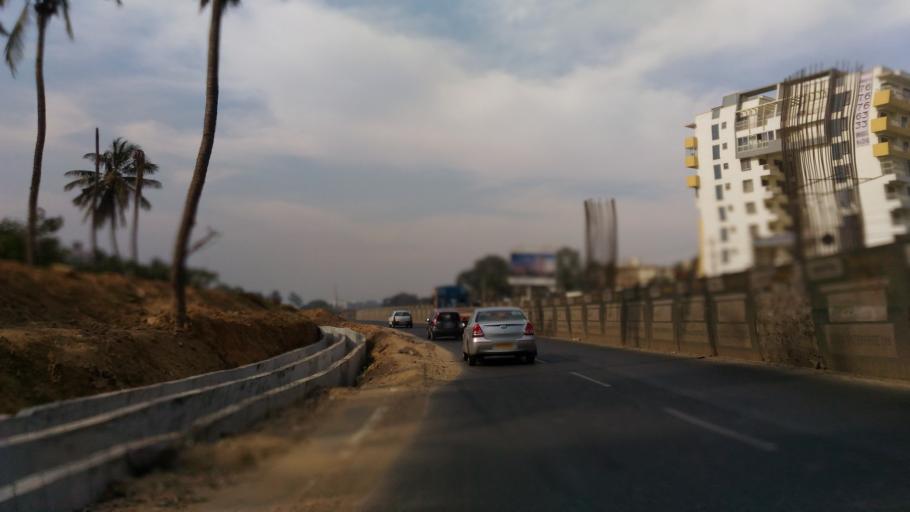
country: IN
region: Karnataka
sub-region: Bangalore Urban
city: Bangalore
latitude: 12.9215
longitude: 77.4938
